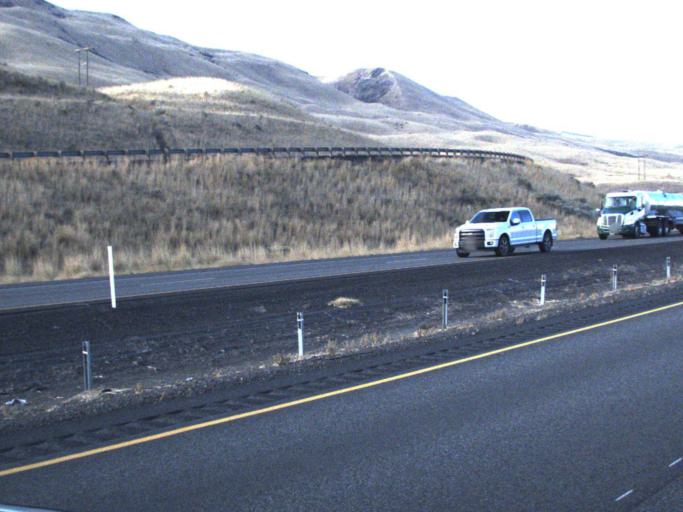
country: US
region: Washington
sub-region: Benton County
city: Benton City
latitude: 46.2493
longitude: -119.6186
